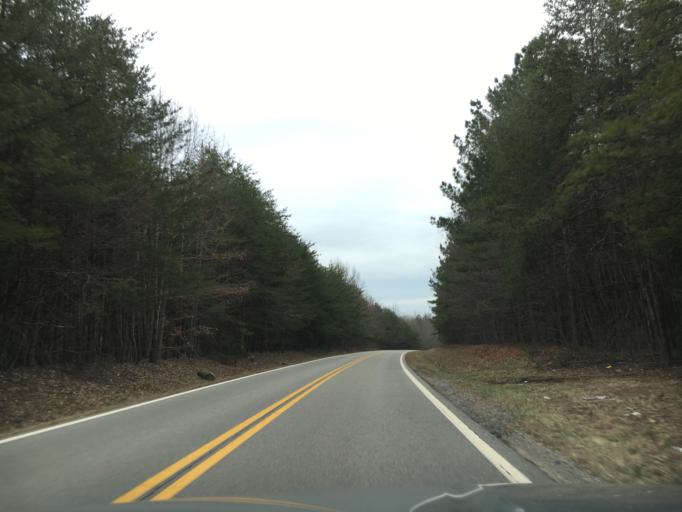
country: US
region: Virginia
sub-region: Charlotte County
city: Charlotte Court House
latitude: 36.9677
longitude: -78.6969
